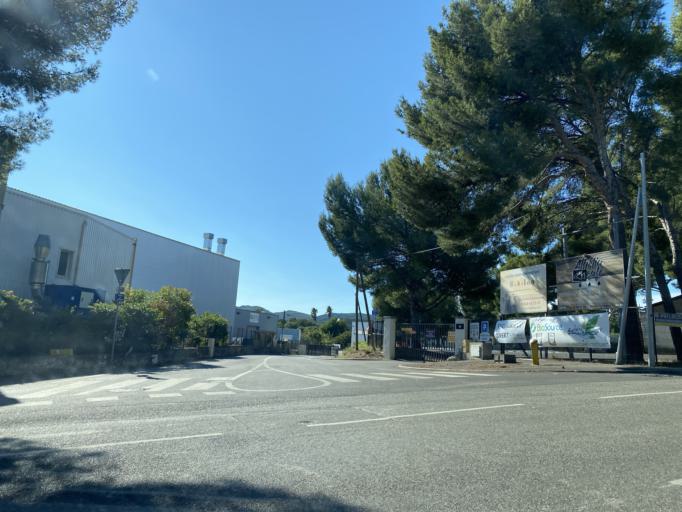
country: FR
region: Provence-Alpes-Cote d'Azur
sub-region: Departement des Bouches-du-Rhone
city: Ceyreste
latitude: 43.2049
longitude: 5.6037
